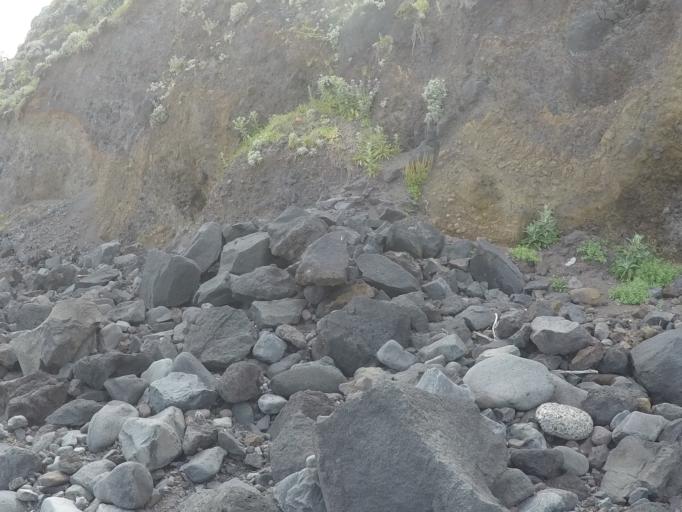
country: PT
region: Madeira
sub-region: Sao Vicente
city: Sao Vicente
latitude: 32.8284
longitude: -16.9948
